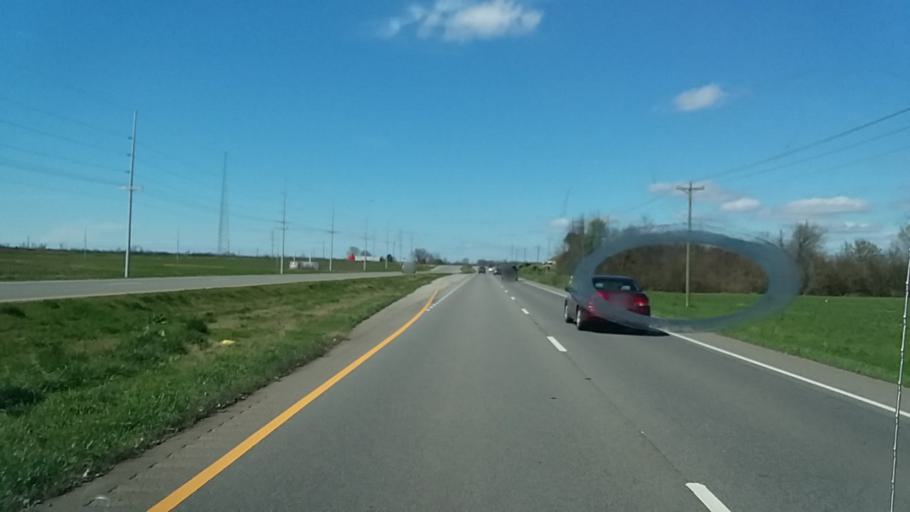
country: US
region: Alabama
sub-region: Morgan County
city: Trinity
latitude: 34.6348
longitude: -87.1079
